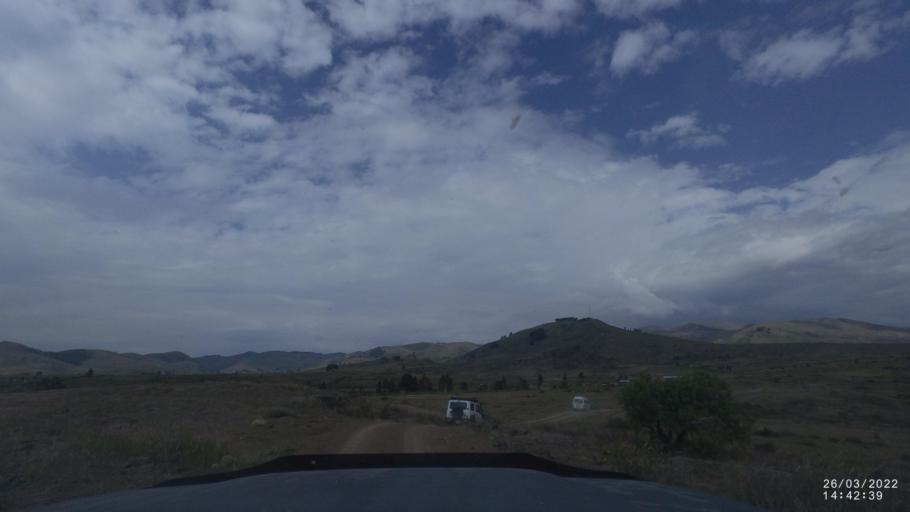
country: BO
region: Cochabamba
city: Cliza
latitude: -17.7375
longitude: -65.8536
